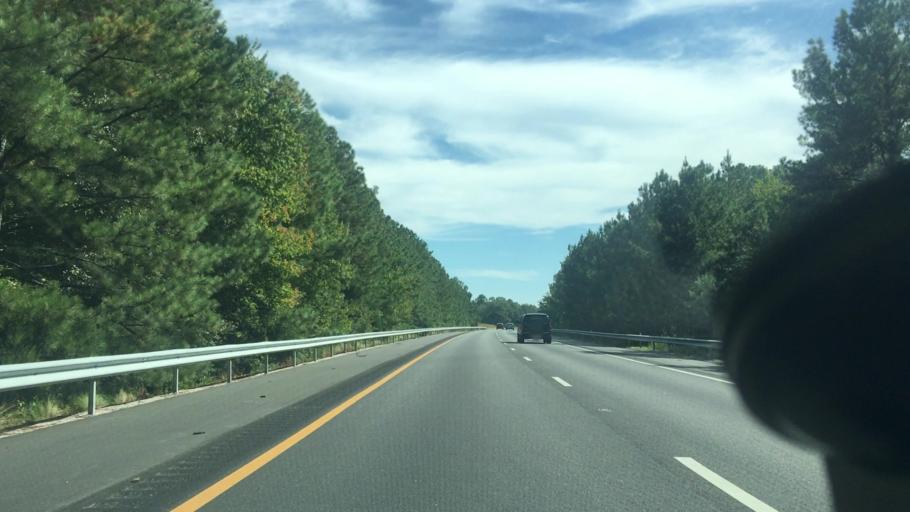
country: US
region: Virginia
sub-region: Chesterfield County
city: Chesterfield
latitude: 37.4044
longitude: -77.5390
